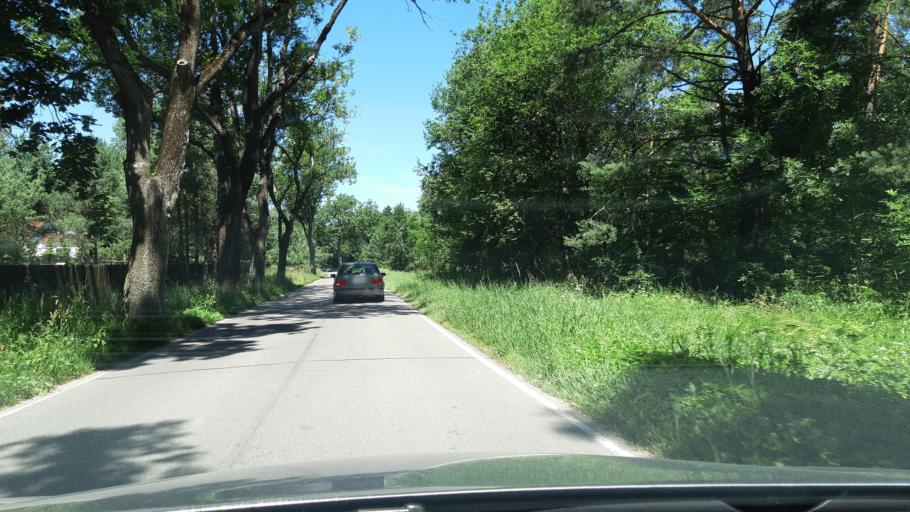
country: PL
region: Warmian-Masurian Voivodeship
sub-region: Powiat gizycki
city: Gizycko
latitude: 53.9419
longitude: 21.7198
